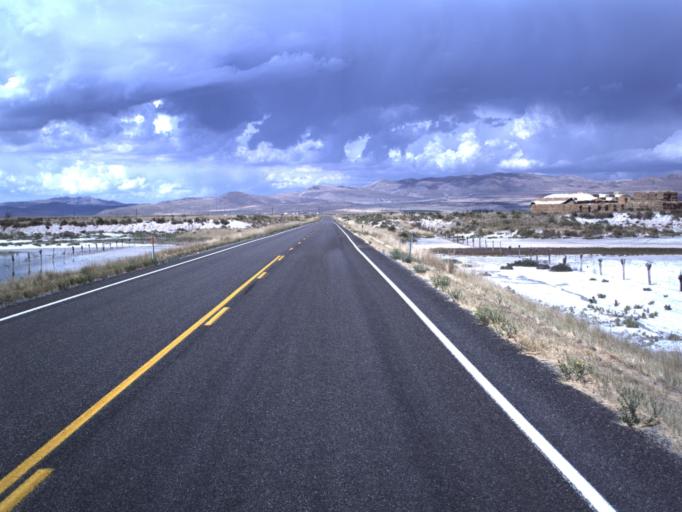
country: US
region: Utah
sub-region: Box Elder County
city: Tremonton
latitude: 41.5833
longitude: -112.2599
